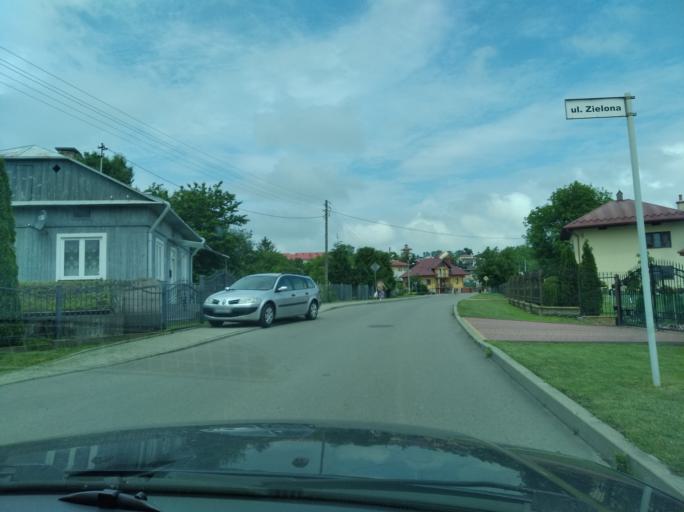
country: PL
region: Subcarpathian Voivodeship
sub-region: Powiat jaroslawski
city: Pruchnik
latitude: 49.9023
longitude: 22.5137
